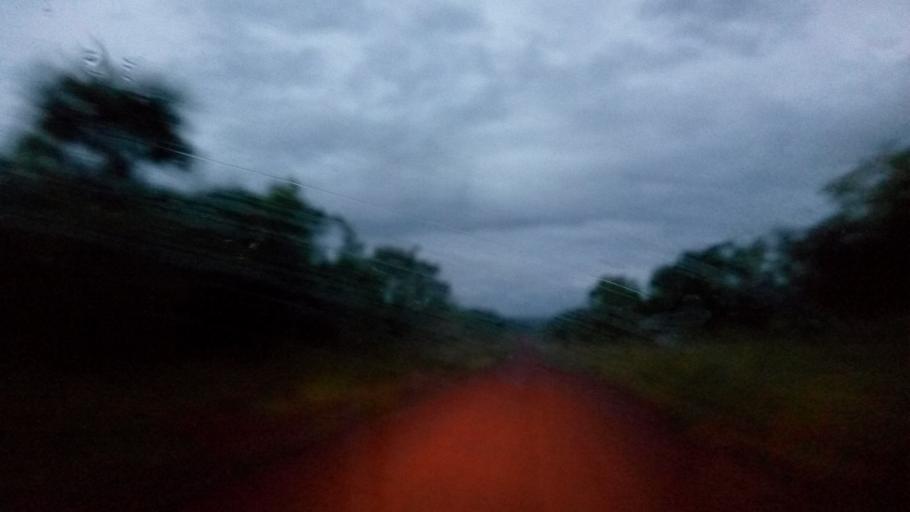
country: ZM
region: Luapula
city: Nchelenge
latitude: -9.7803
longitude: 28.1694
